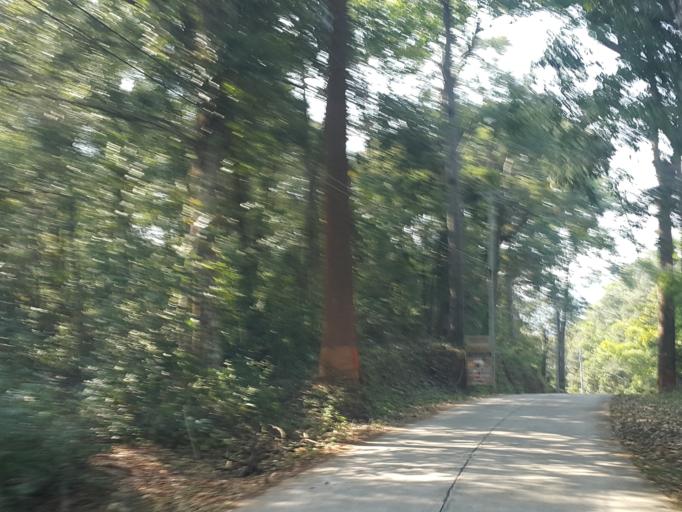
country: TH
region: Chiang Mai
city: Samoeng
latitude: 19.0236
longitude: 98.7805
